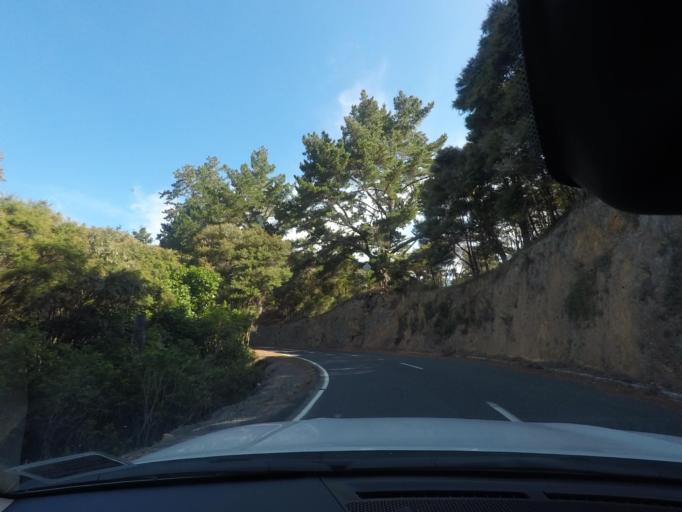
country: NZ
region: Northland
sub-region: Whangarei
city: Ngunguru
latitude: -35.6710
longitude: 174.4582
